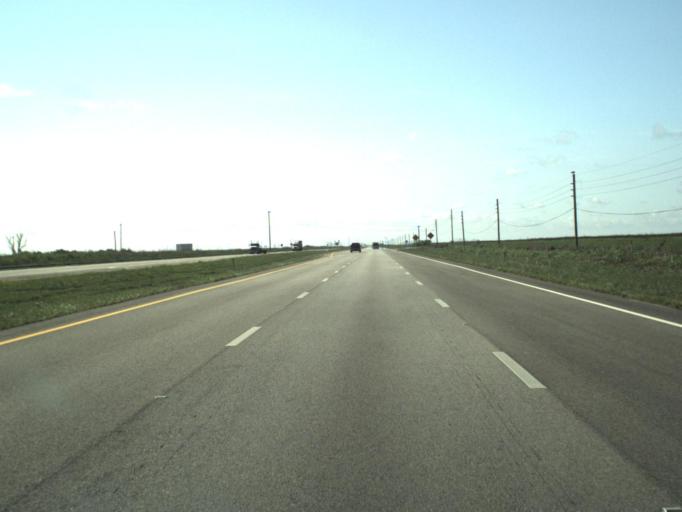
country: US
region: Florida
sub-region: Palm Beach County
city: Belle Glade Camp
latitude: 26.3880
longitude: -80.5791
